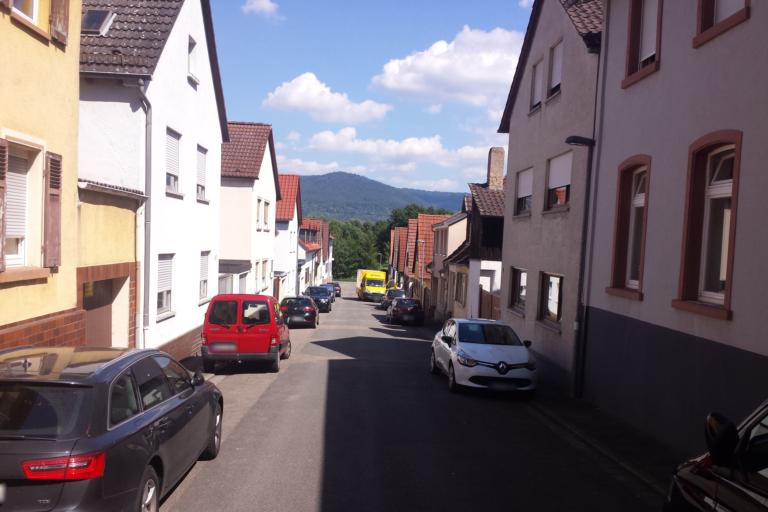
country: DE
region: Baden-Wuerttemberg
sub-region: Karlsruhe Region
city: Eppelheim
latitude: 49.4261
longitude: 8.6494
